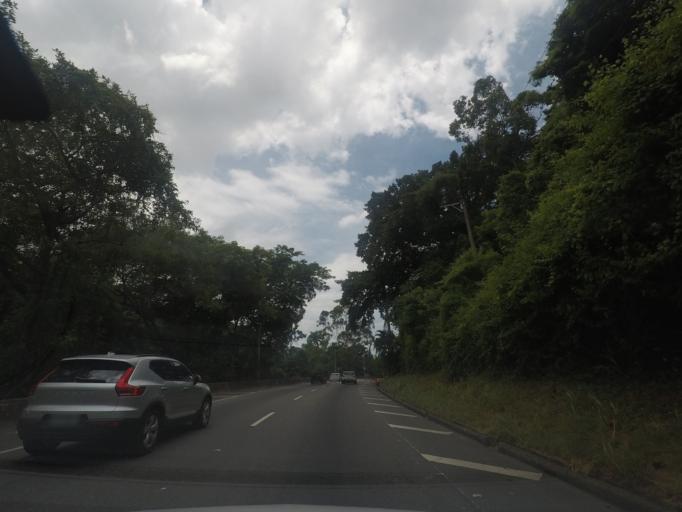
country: BR
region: Rio de Janeiro
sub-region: Rio De Janeiro
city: Rio de Janeiro
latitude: -22.9833
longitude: -43.2376
